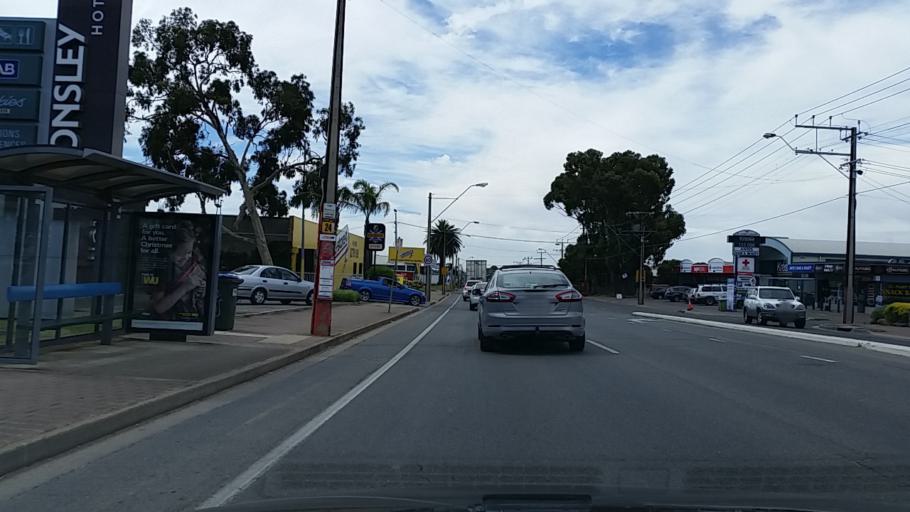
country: AU
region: South Australia
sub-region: Marion
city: Clovelly Park
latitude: -35.0047
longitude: 138.5757
